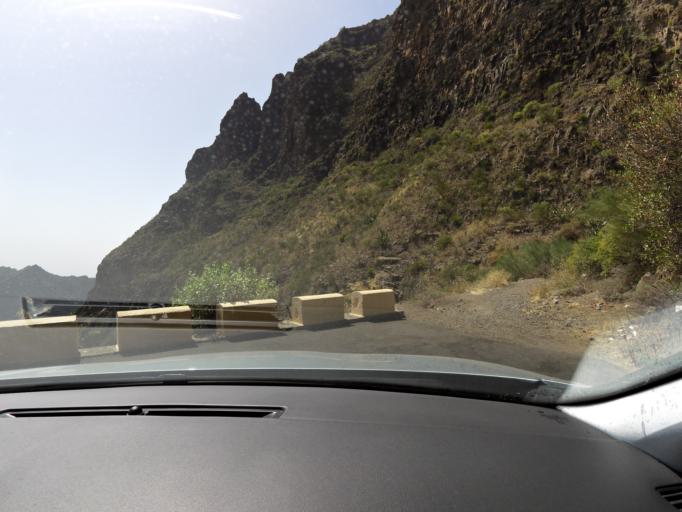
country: ES
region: Canary Islands
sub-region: Provincia de Santa Cruz de Tenerife
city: Santiago del Teide
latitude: 28.3045
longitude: -16.8298
